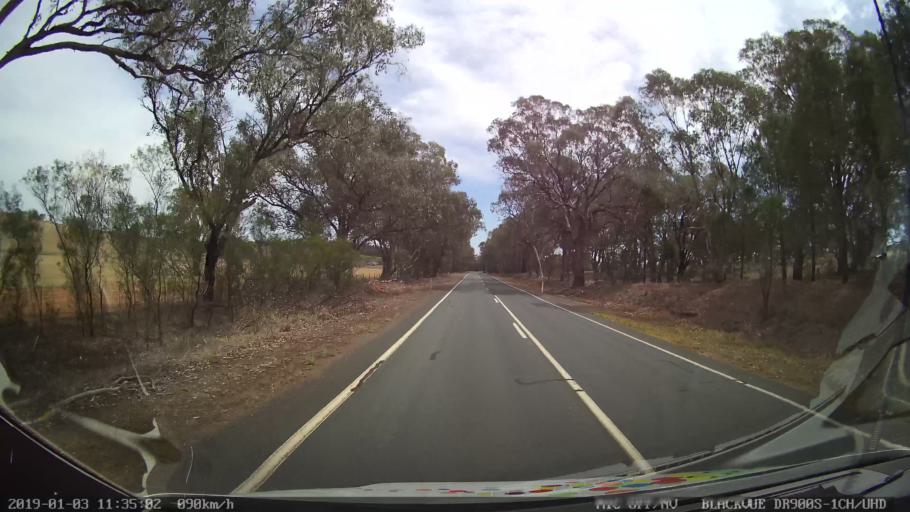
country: AU
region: New South Wales
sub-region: Weddin
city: Grenfell
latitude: -33.9277
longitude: 148.1601
